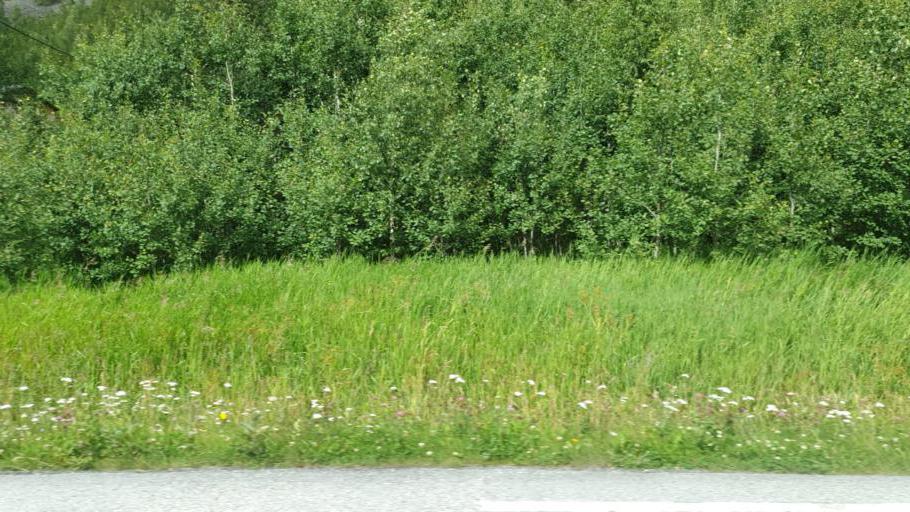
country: NO
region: Oppland
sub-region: Sel
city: Otta
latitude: 61.8434
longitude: 9.3789
